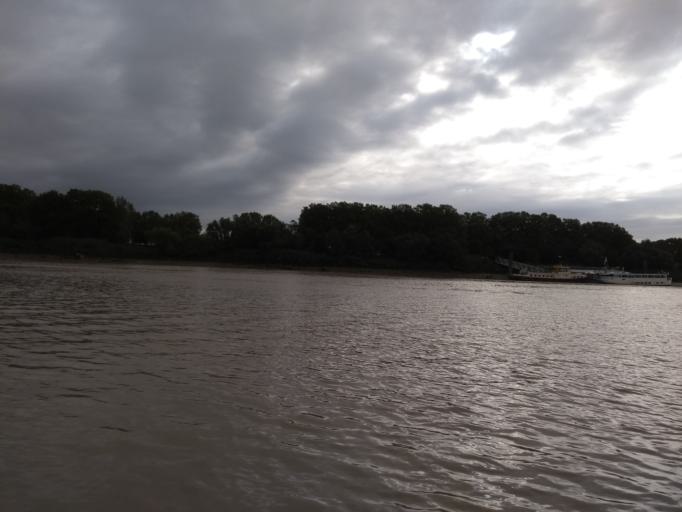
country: FR
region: Aquitaine
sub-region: Departement de la Gironde
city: Bordeaux
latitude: 44.8456
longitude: -0.5684
